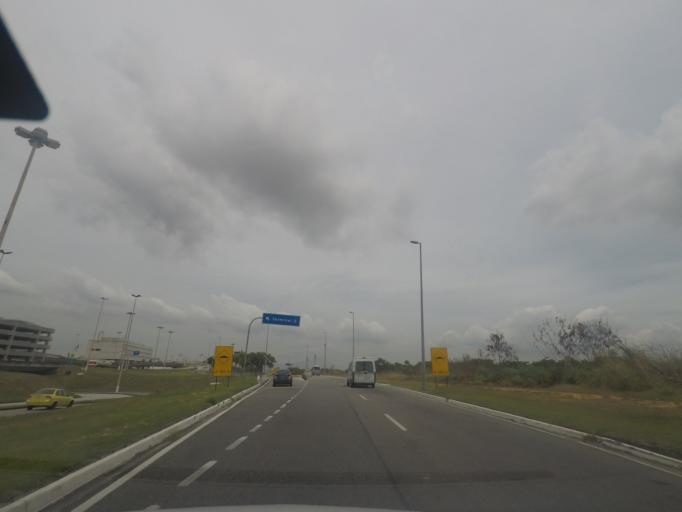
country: BR
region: Rio de Janeiro
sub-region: Duque De Caxias
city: Duque de Caxias
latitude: -22.8135
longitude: -43.2442
